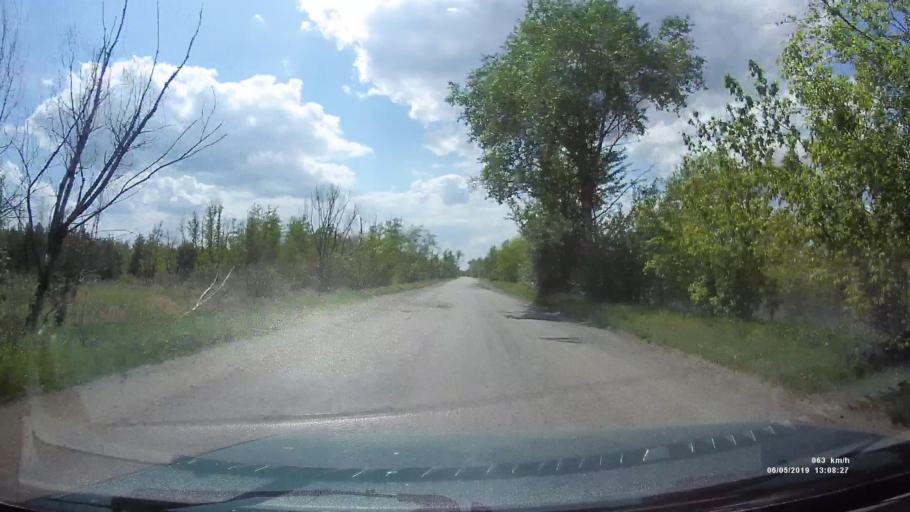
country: RU
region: Rostov
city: Ust'-Donetskiy
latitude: 47.7755
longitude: 40.9953
